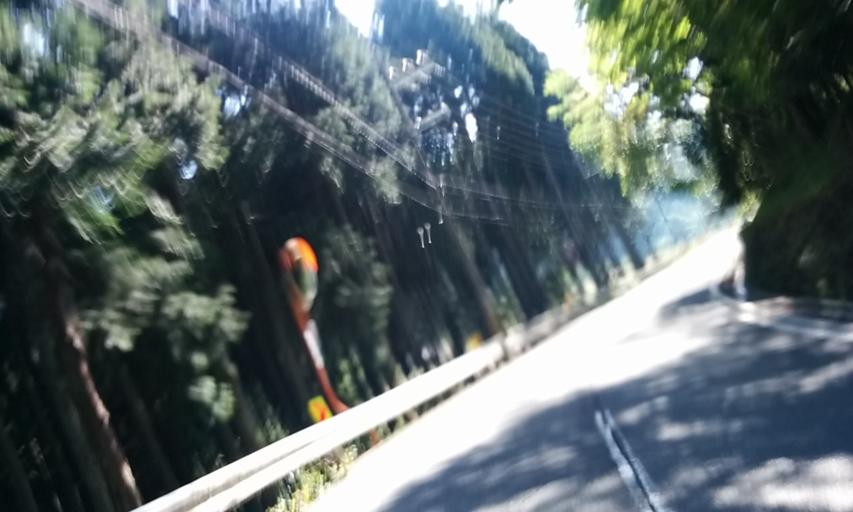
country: JP
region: Kyoto
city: Ayabe
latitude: 35.2596
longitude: 135.4564
